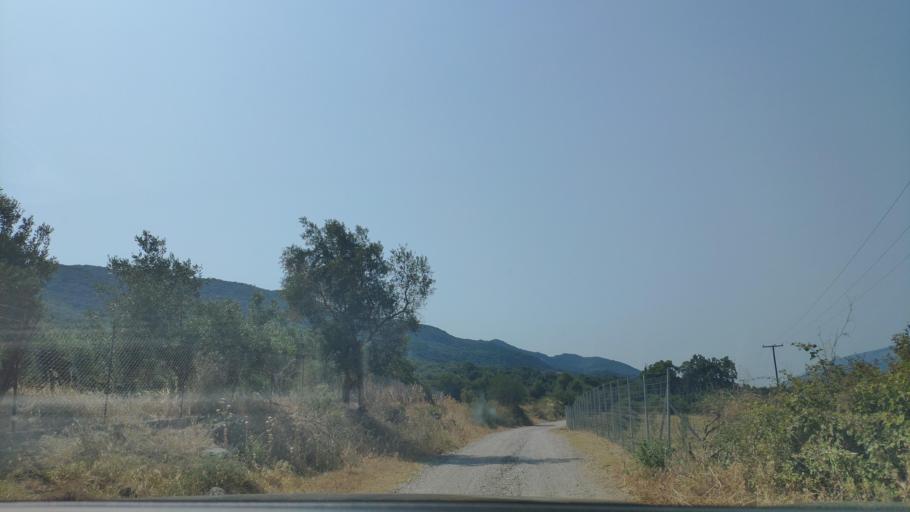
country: GR
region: West Greece
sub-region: Nomos Aitolias kai Akarnanias
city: Fitiai
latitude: 38.7146
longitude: 21.2007
